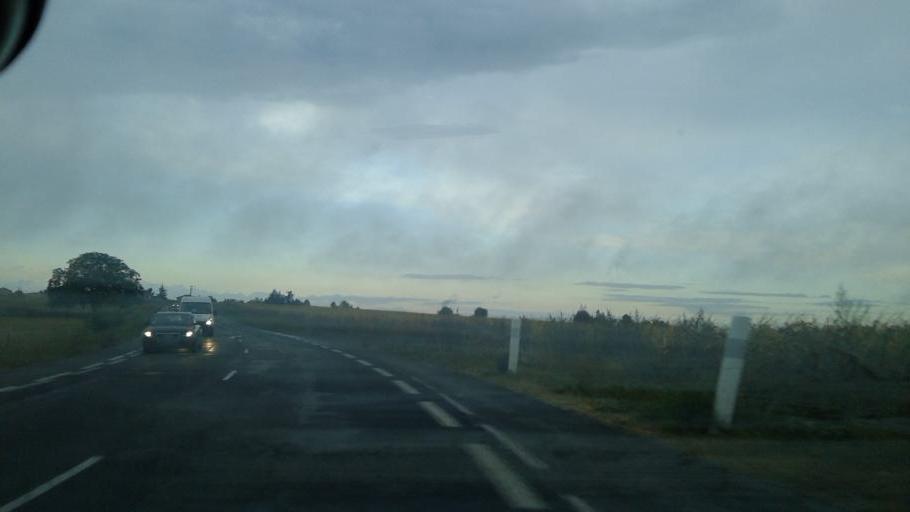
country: FR
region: Rhone-Alpes
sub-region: Departement de l'Ain
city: Miribel
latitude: 45.8280
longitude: 4.9365
